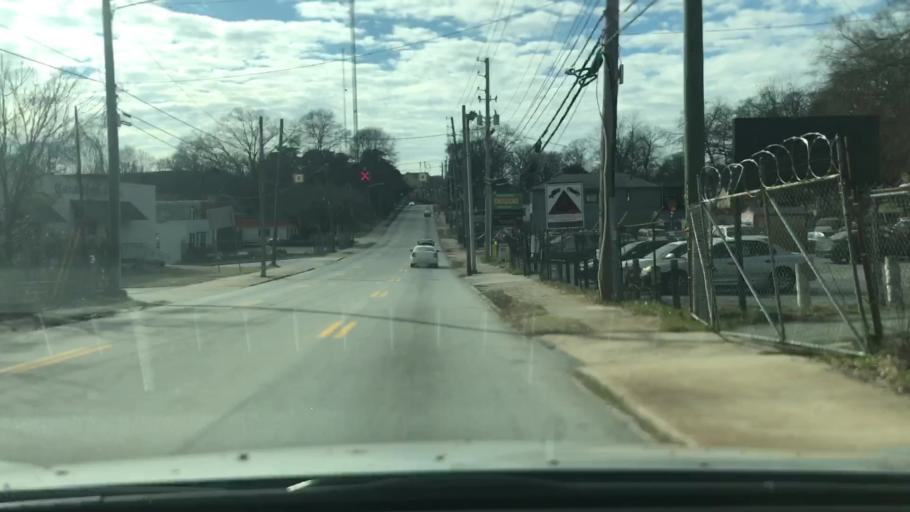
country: US
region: Georgia
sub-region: DeKalb County
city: Druid Hills
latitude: 33.7473
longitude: -84.3511
